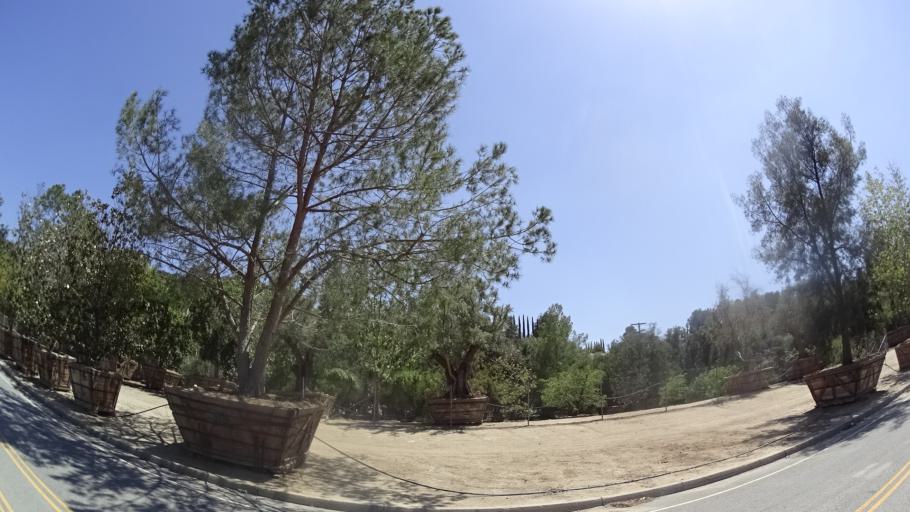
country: US
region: California
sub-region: Los Angeles County
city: La Crescenta-Montrose
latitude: 34.2763
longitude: -118.3018
